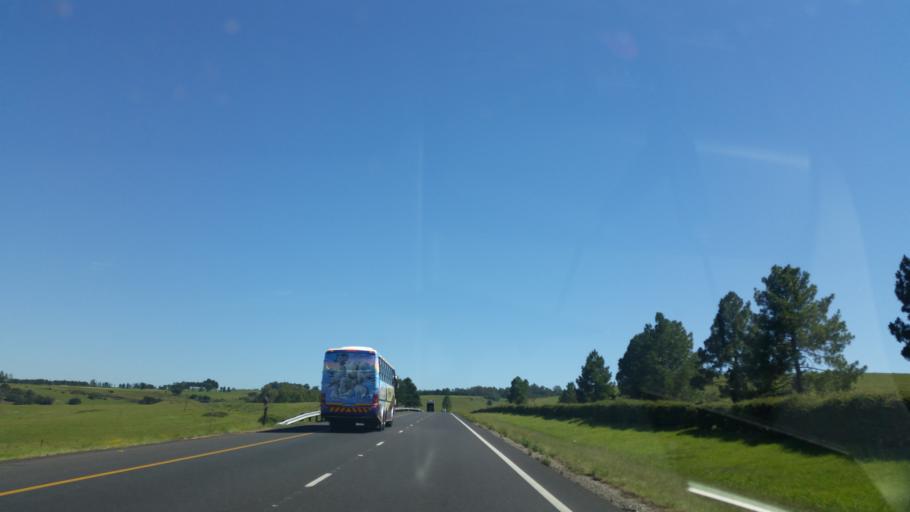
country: ZA
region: KwaZulu-Natal
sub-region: uMgungundlovu District Municipality
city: Mooirivier
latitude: -29.1681
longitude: 29.9834
